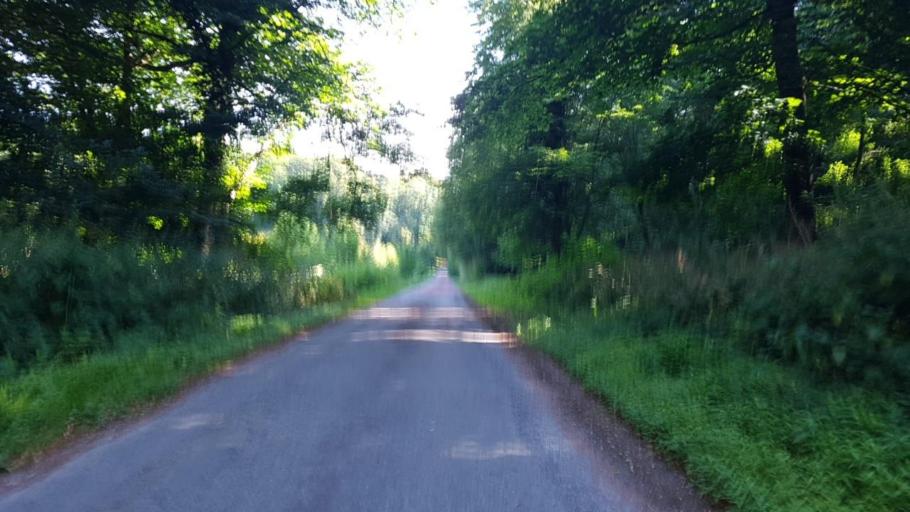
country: FR
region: Picardie
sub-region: Departement de l'Oise
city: Chamant
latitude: 49.2497
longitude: 2.6146
